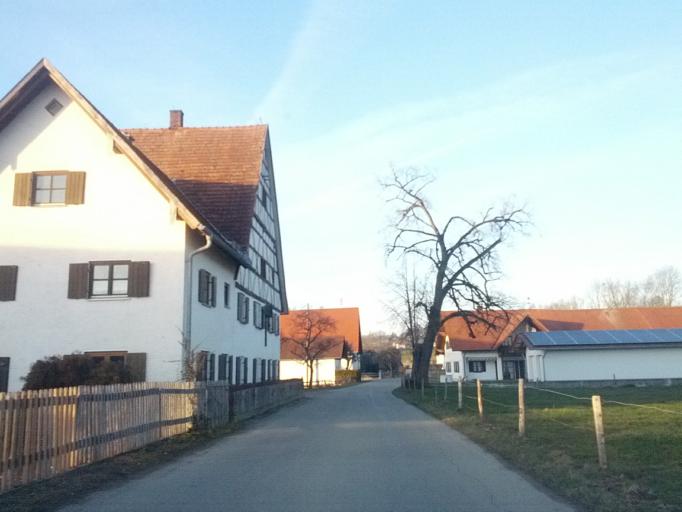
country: DE
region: Bavaria
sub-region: Swabia
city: Kronburg
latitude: 47.8870
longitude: 10.1616
